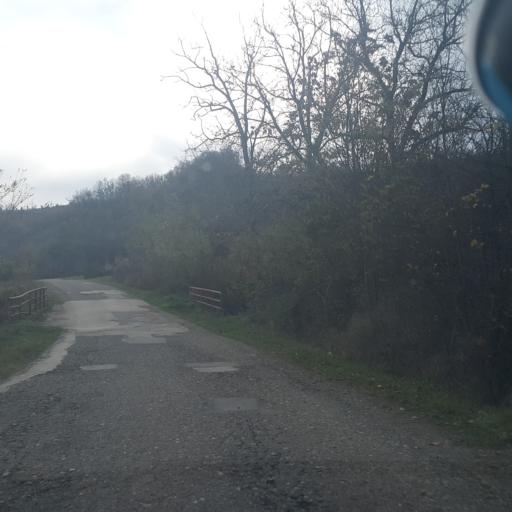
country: RS
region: Central Serbia
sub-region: Zajecarski Okrug
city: Knjazevac
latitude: 43.6085
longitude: 22.2590
